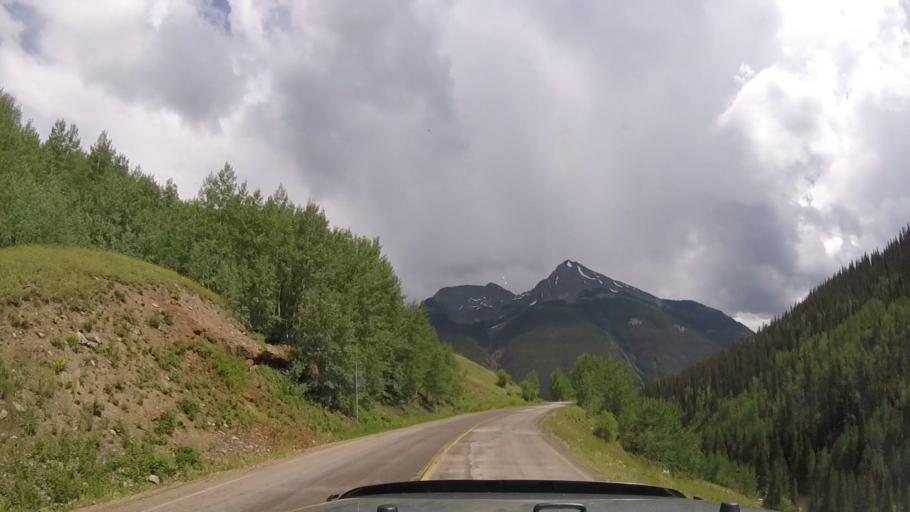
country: US
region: Colorado
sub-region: San Juan County
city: Silverton
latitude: 37.8227
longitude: -107.6650
